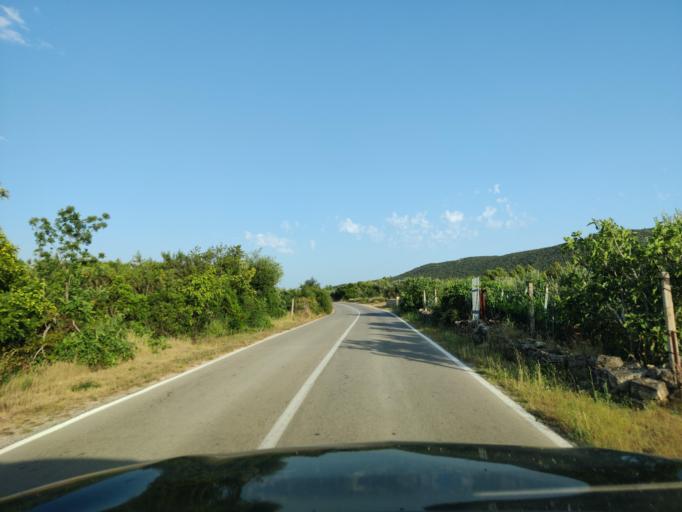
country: HR
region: Sibensko-Kniniska
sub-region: Grad Sibenik
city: Pirovac
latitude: 43.7917
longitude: 15.6929
